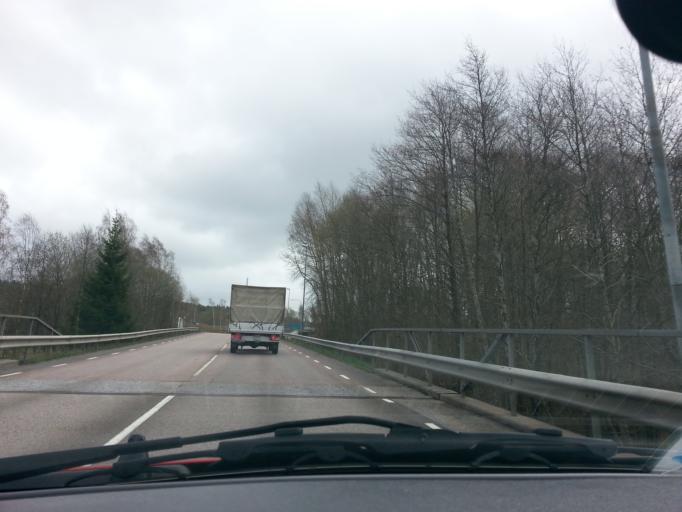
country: SE
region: Vaestra Goetaland
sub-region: Lerums Kommun
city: Lerum
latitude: 57.7752
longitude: 12.2893
